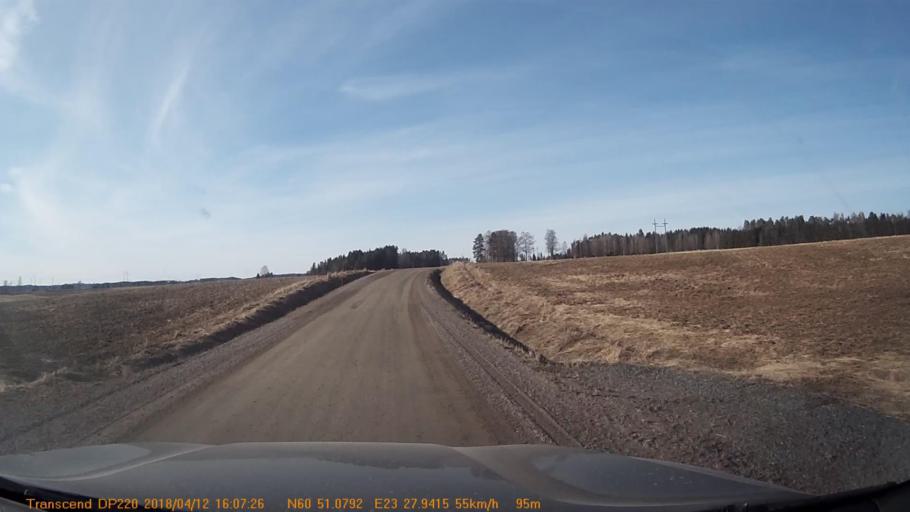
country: FI
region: Haeme
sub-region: Forssa
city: Jokioinen
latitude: 60.8514
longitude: 23.4655
